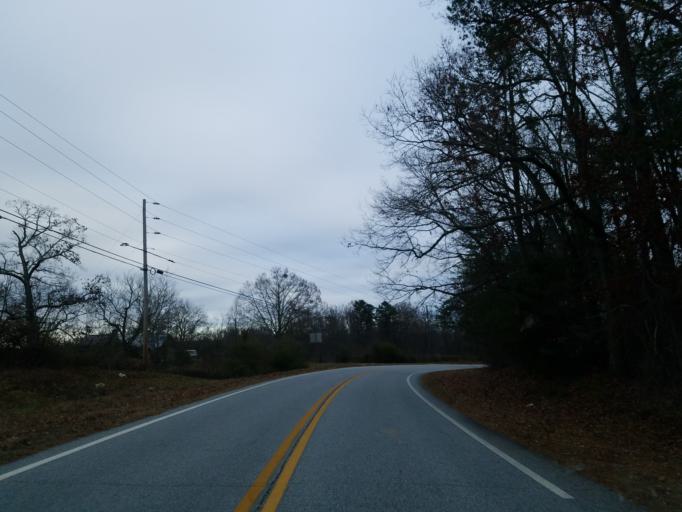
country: US
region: Georgia
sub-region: Dawson County
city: Dawsonville
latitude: 34.3974
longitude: -84.0112
